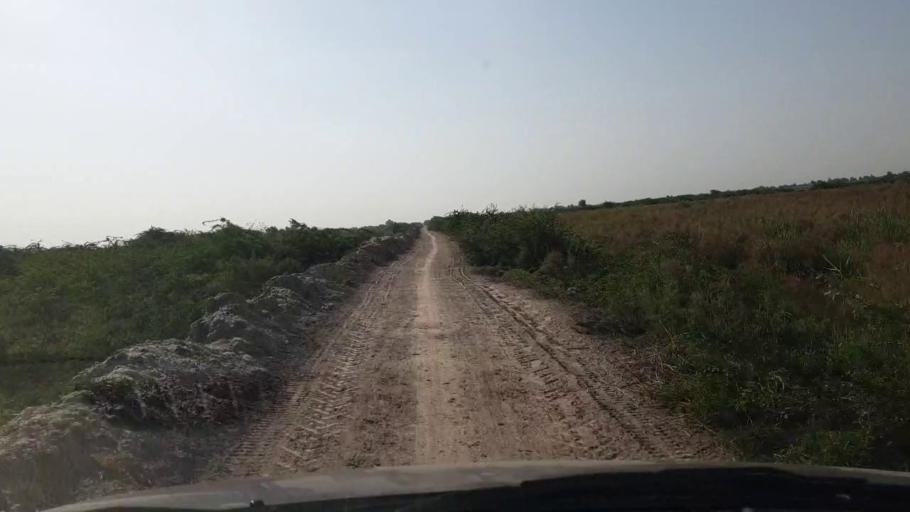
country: PK
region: Sindh
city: Kadhan
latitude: 24.6076
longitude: 69.0735
